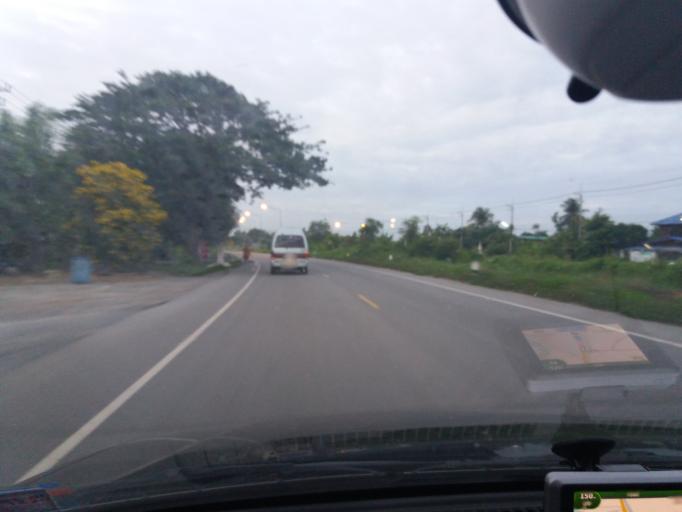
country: TH
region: Suphan Buri
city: Ban Sam Chuk
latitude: 14.7378
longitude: 100.0928
